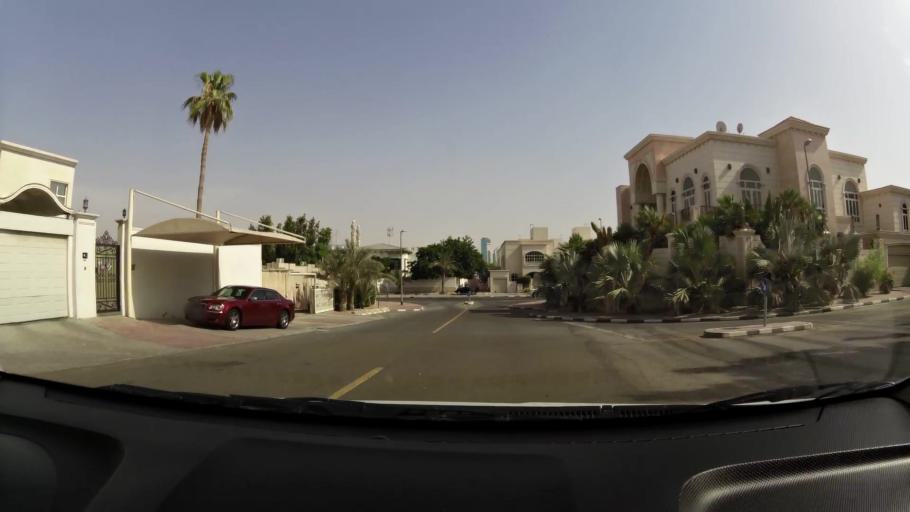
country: AE
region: Ash Shariqah
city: Sharjah
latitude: 25.2412
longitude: 55.3501
